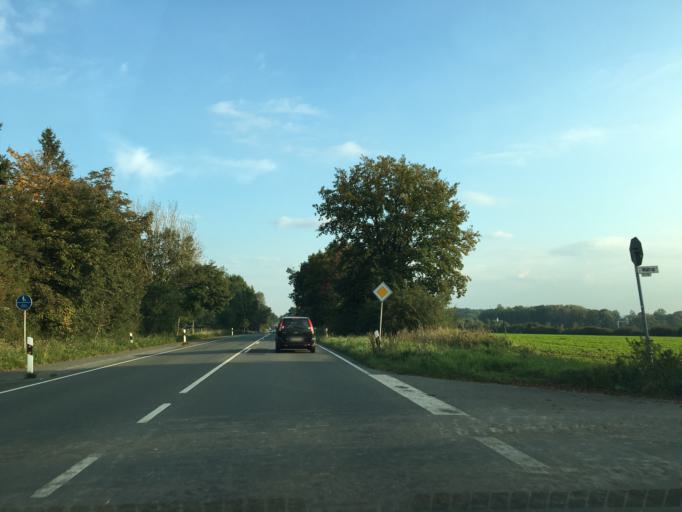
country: DE
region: North Rhine-Westphalia
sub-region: Regierungsbezirk Munster
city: Altenberge
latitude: 52.0323
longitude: 7.4827
